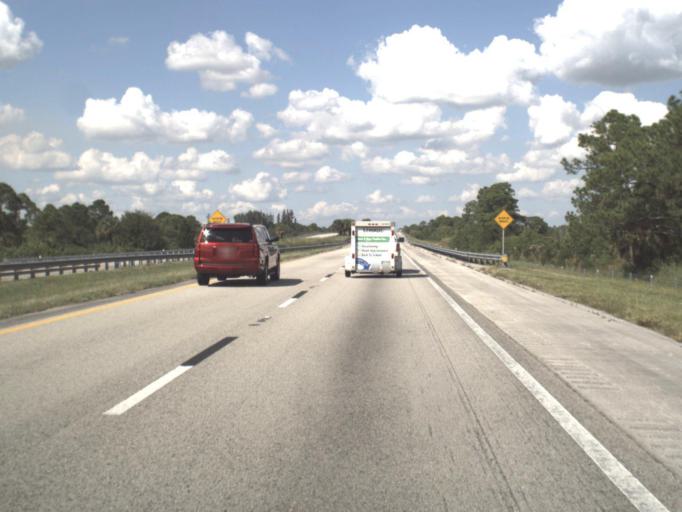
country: US
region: Florida
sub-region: Saint Lucie County
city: Lakewood Park
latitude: 27.4663
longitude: -80.4389
